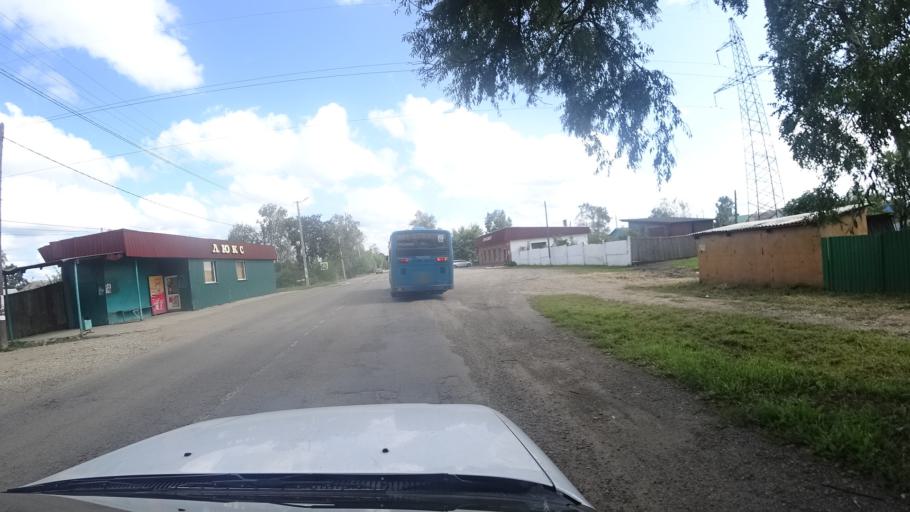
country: RU
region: Primorskiy
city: Dal'nerechensk
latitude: 45.9277
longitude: 133.7661
